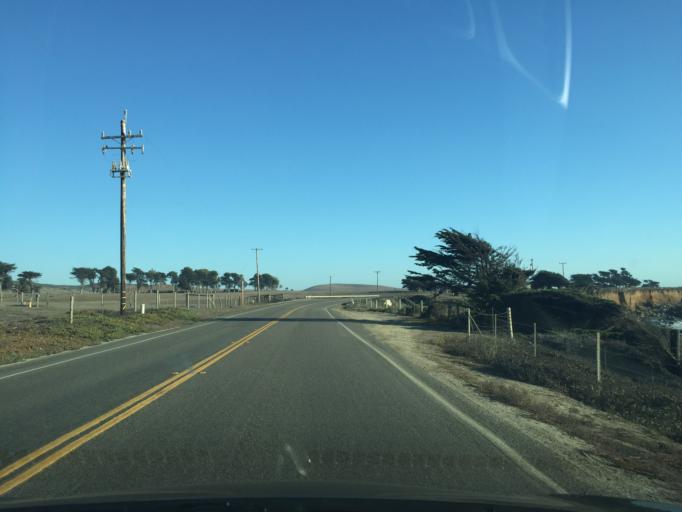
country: US
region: California
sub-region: San Luis Obispo County
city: Cambria
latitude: 35.6909
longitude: -121.2893
